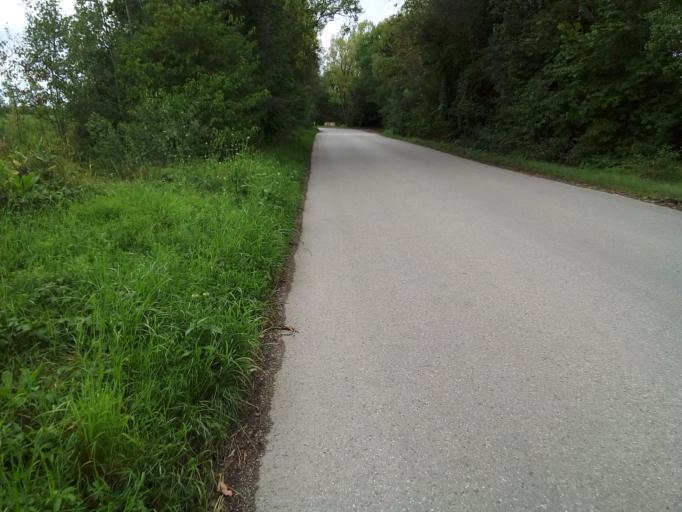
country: DE
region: Bavaria
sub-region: Upper Bavaria
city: Aschheim
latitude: 48.1563
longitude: 11.6970
